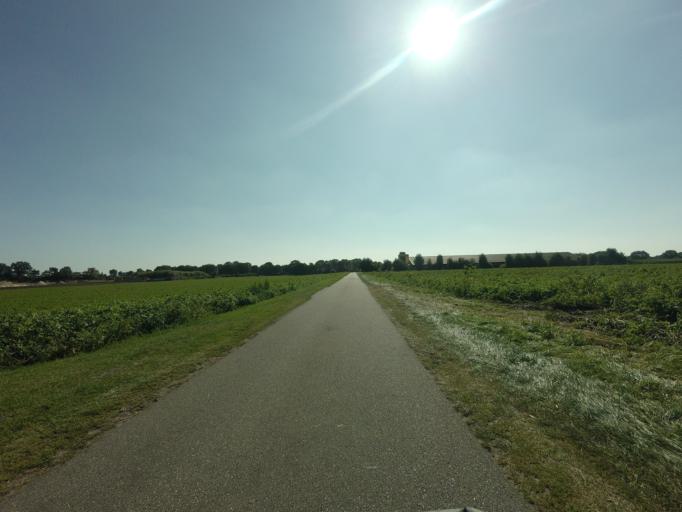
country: DE
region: Lower Saxony
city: Wielen
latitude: 52.5247
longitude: 6.7083
